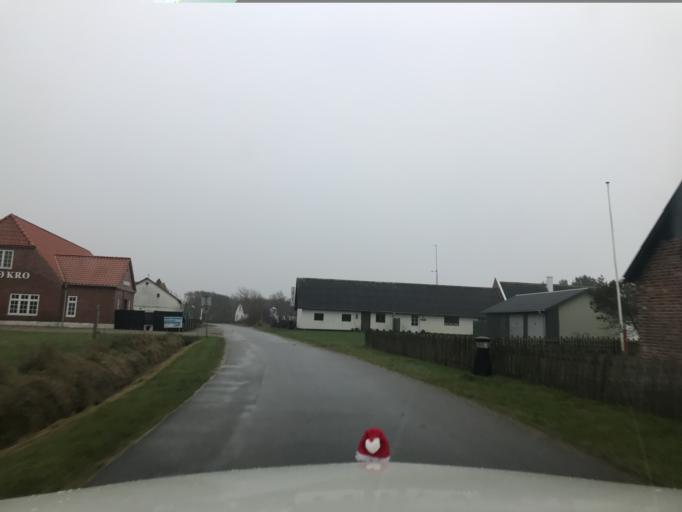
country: DK
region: South Denmark
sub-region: Esbjerg Kommune
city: Tjaereborg
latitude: 55.2770
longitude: 8.5369
